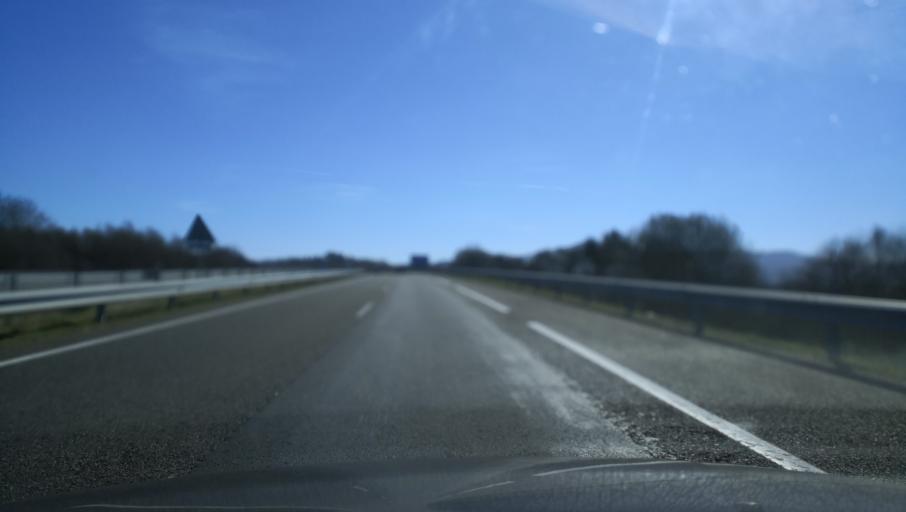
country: ES
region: Galicia
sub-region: Provincia de Ourense
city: Taboadela
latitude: 42.2118
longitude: -7.8352
